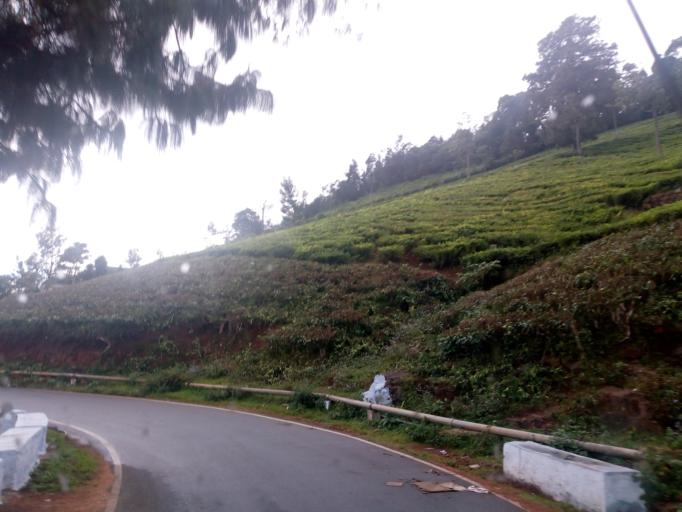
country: IN
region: Tamil Nadu
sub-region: Nilgiri
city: Wellington
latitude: 11.3538
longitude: 76.8315
